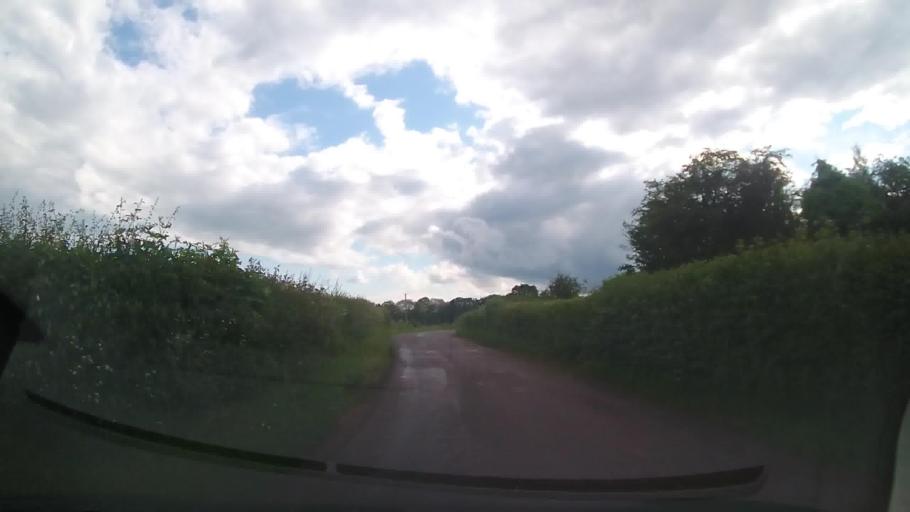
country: GB
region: England
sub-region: Telford and Wrekin
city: Wellington
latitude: 52.6588
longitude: -2.5171
